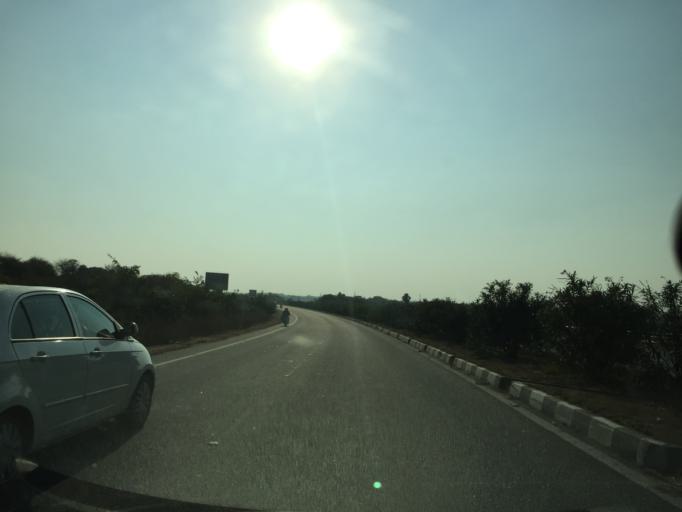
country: IN
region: Telangana
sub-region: Nalgonda
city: Bhongir
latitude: 17.5124
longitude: 78.9020
